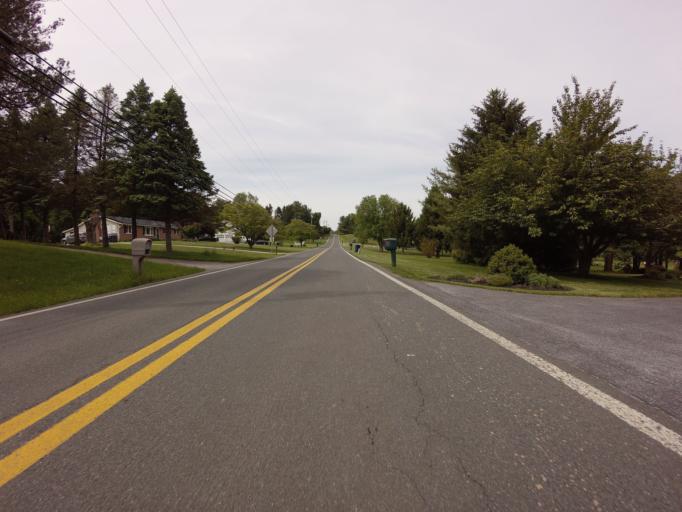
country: US
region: Maryland
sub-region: Carroll County
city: Eldersburg
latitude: 39.4606
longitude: -76.9537
